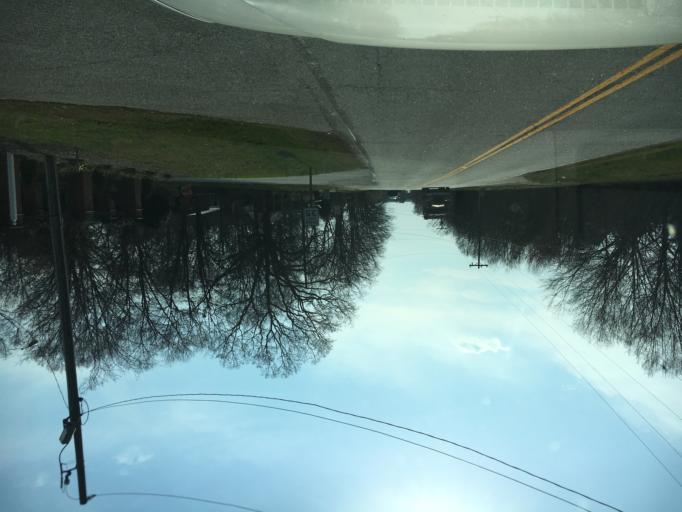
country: US
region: South Carolina
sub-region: Spartanburg County
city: Mayo
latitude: 35.1536
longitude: -81.8534
